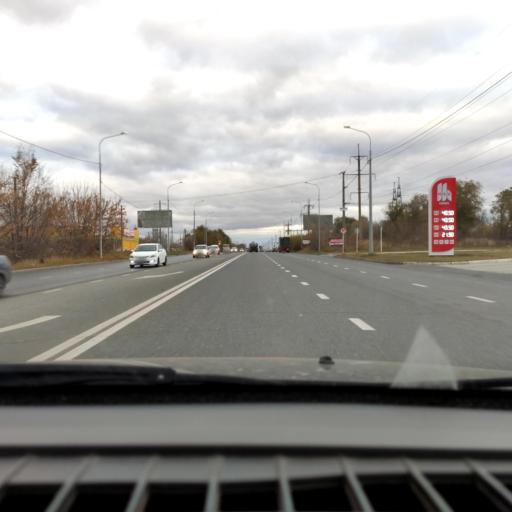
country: RU
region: Samara
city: Tol'yatti
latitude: 53.5680
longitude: 49.2913
